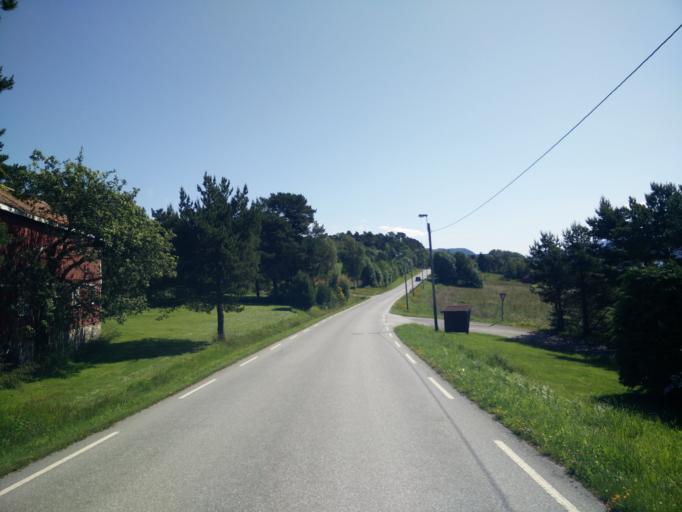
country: NO
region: More og Romsdal
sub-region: Kristiansund
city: Rensvik
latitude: 63.0288
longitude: 7.7829
